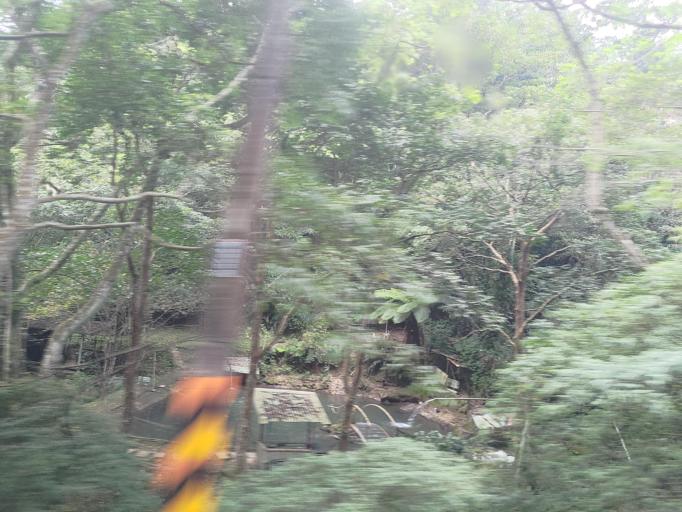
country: TW
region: Taiwan
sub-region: Hsinchu
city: Hsinchu
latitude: 24.6143
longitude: 121.0426
